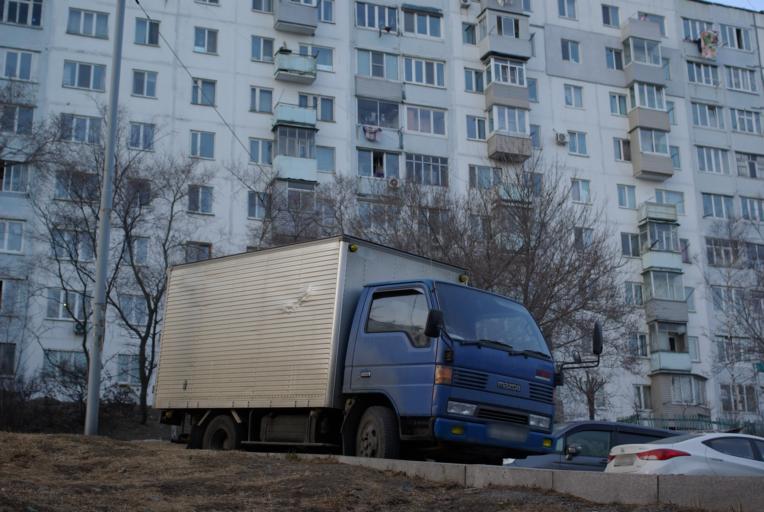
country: RU
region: Primorskiy
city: Vladivostok
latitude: 43.0964
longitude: 131.9076
